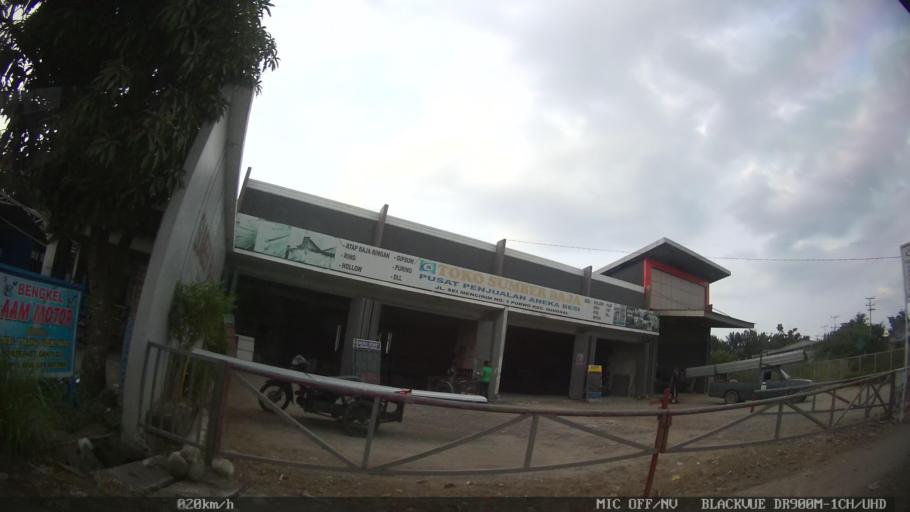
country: ID
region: North Sumatra
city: Sunggal
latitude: 3.5614
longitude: 98.5656
